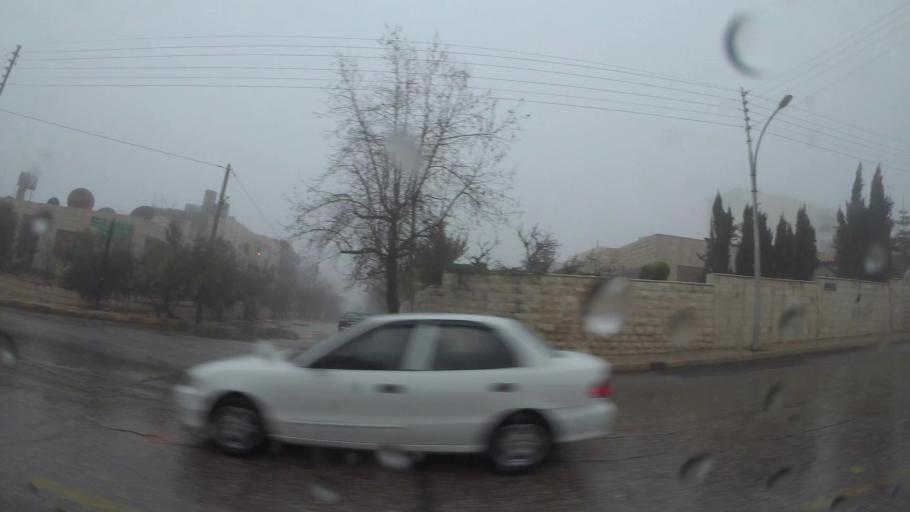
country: JO
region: Amman
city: Al Jubayhah
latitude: 32.0121
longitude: 35.8827
